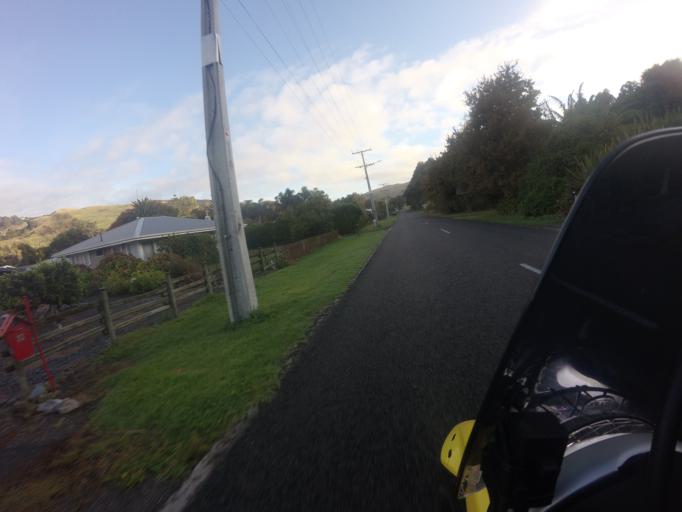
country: NZ
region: Gisborne
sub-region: Gisborne District
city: Gisborne
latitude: -38.6739
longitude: 178.0805
